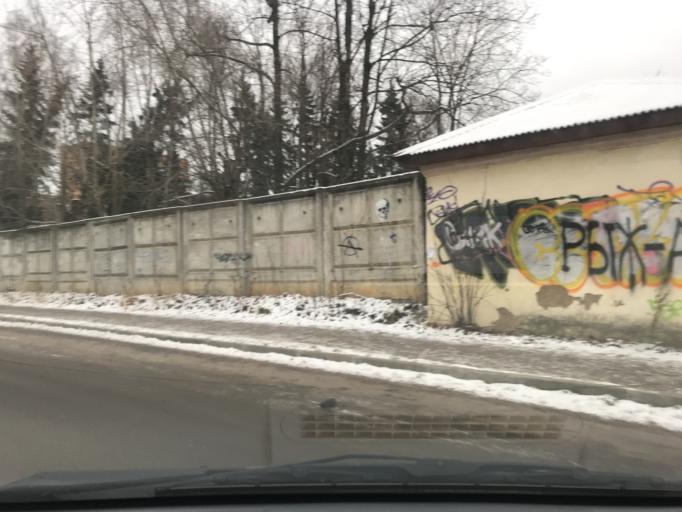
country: RU
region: Moskovskaya
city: Elektrostal'
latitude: 55.8042
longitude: 38.4649
